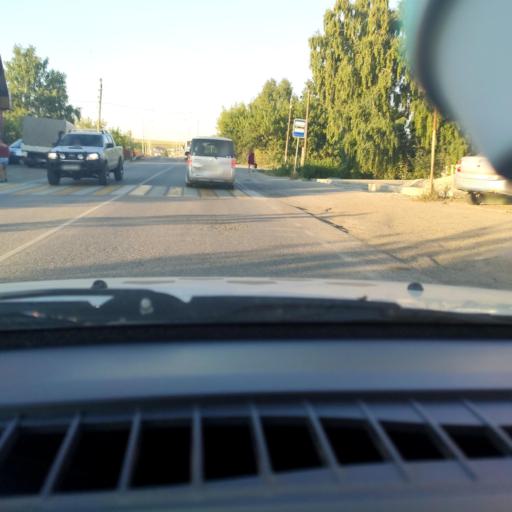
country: RU
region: Perm
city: Kungur
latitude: 57.4283
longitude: 57.0165
